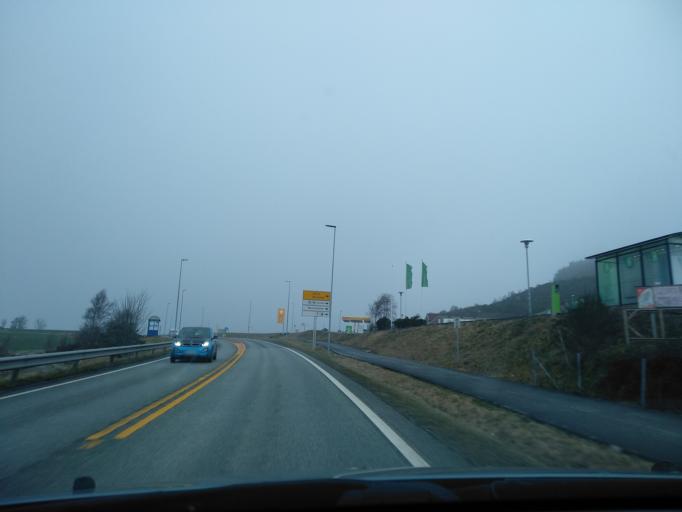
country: NO
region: Rogaland
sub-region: Rennesoy
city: Vikevag
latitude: 59.0630
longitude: 5.6771
